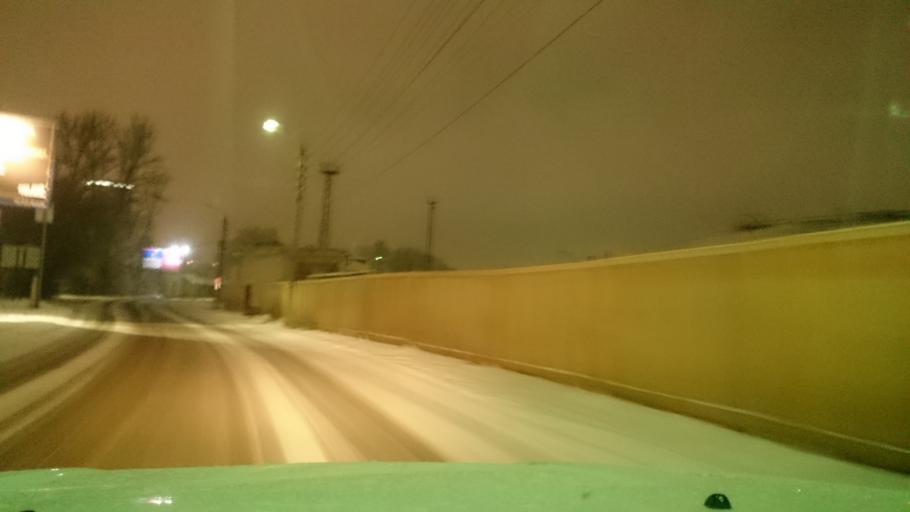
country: RU
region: Tula
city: Tula
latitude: 54.1953
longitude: 37.5761
